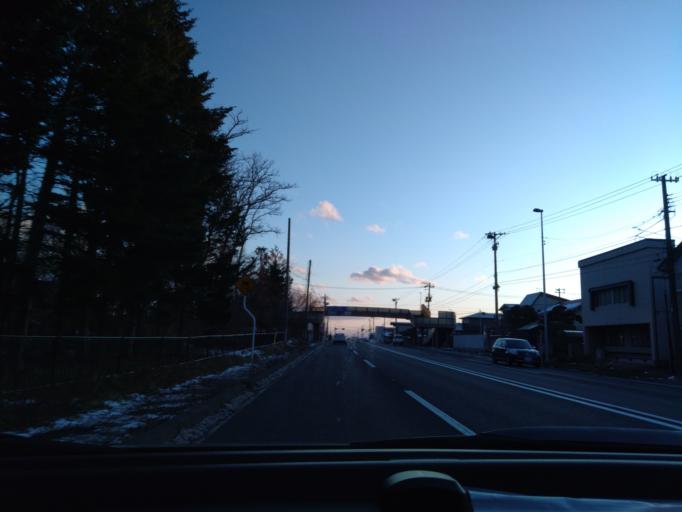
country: JP
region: Iwate
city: Hanamaki
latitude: 39.4232
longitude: 141.1295
